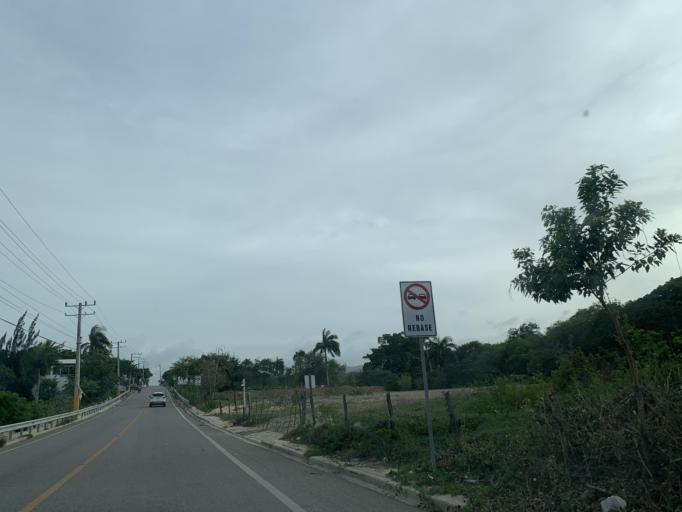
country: DO
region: Puerto Plata
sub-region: Puerto Plata
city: Puerto Plata
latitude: 19.7167
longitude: -70.6204
